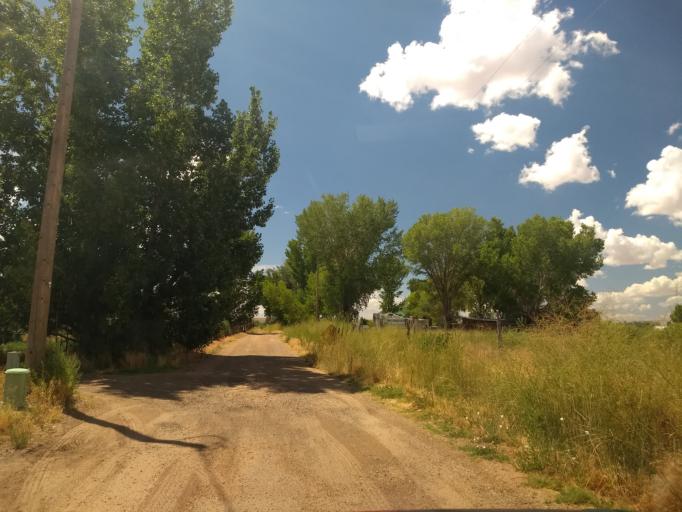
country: US
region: Arizona
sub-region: Coconino County
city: Fredonia
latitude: 36.9396
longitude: -112.5308
